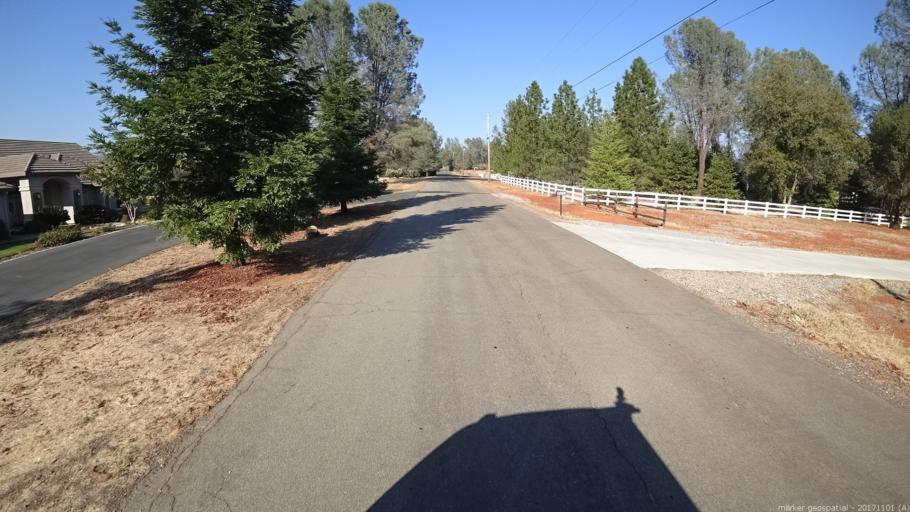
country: US
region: California
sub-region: Shasta County
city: Shasta Lake
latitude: 40.6775
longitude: -122.3441
